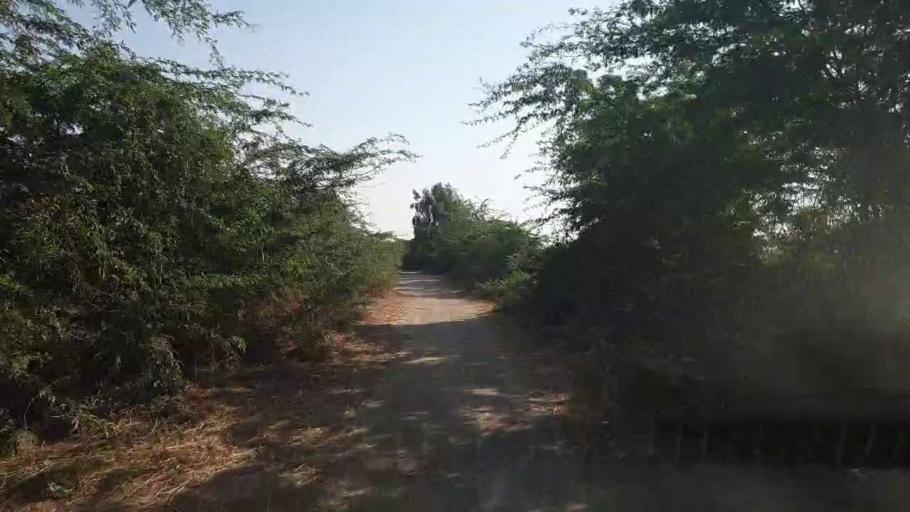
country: PK
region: Sindh
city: Matli
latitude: 25.0092
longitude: 68.7406
